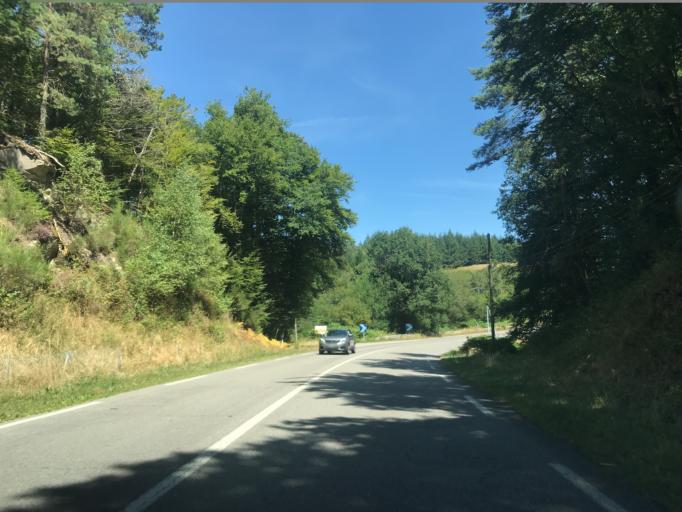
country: FR
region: Limousin
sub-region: Departement de la Correze
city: Egletons
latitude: 45.3553
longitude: 1.9702
